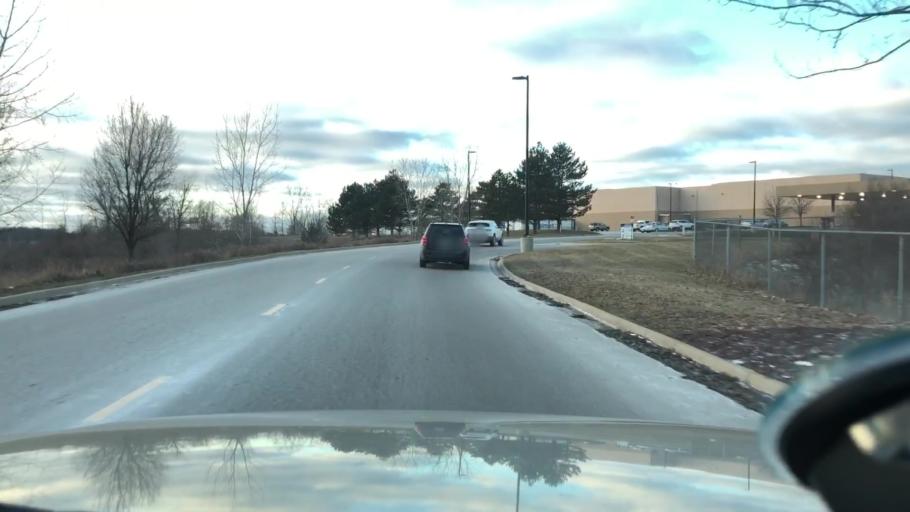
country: US
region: Michigan
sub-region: Jackson County
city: Jackson
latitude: 42.2659
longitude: -84.4602
